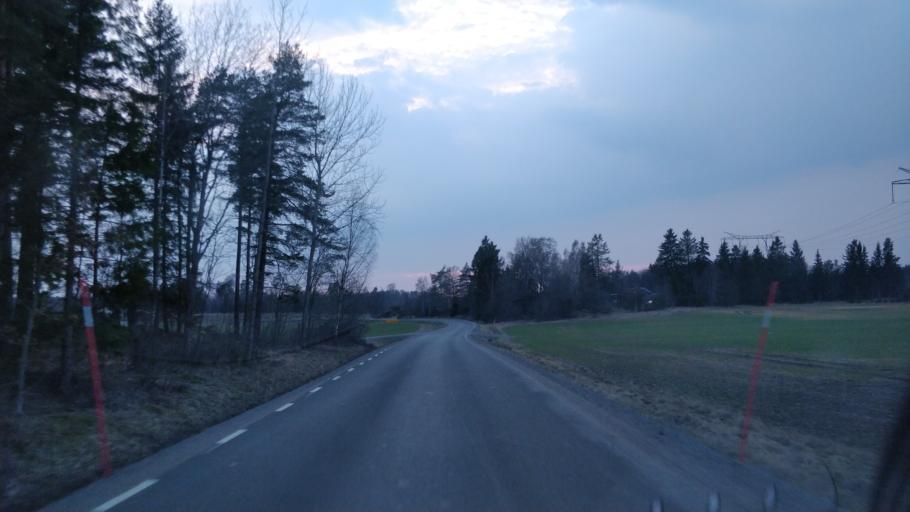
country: SE
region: Uppsala
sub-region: Enkopings Kommun
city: Orsundsbro
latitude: 59.7248
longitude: 17.2784
